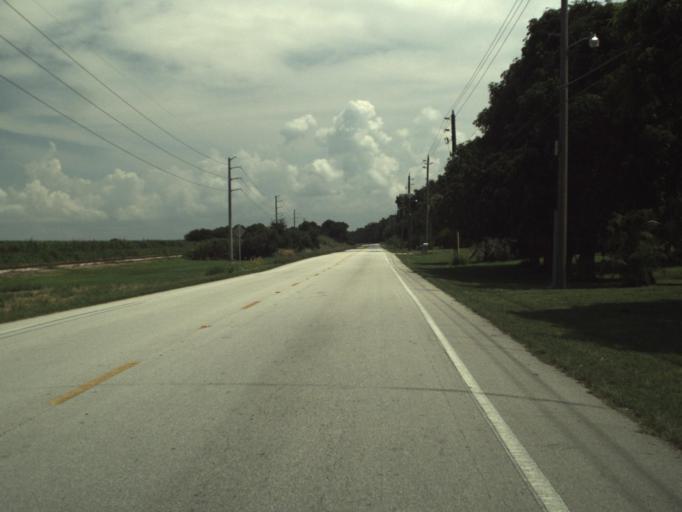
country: US
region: Florida
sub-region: Palm Beach County
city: Pahokee
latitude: 26.8798
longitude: -80.6196
